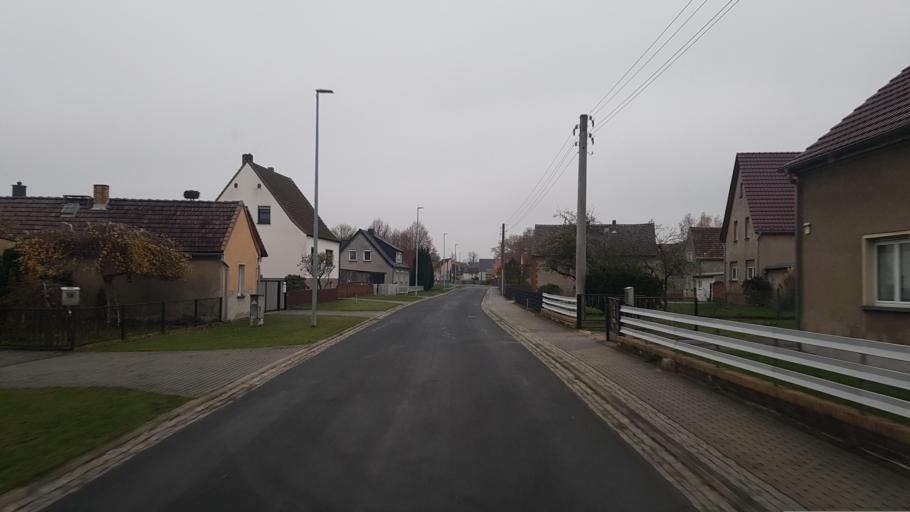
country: DE
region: Brandenburg
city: Hermsdorf
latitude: 51.4065
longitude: 13.8931
